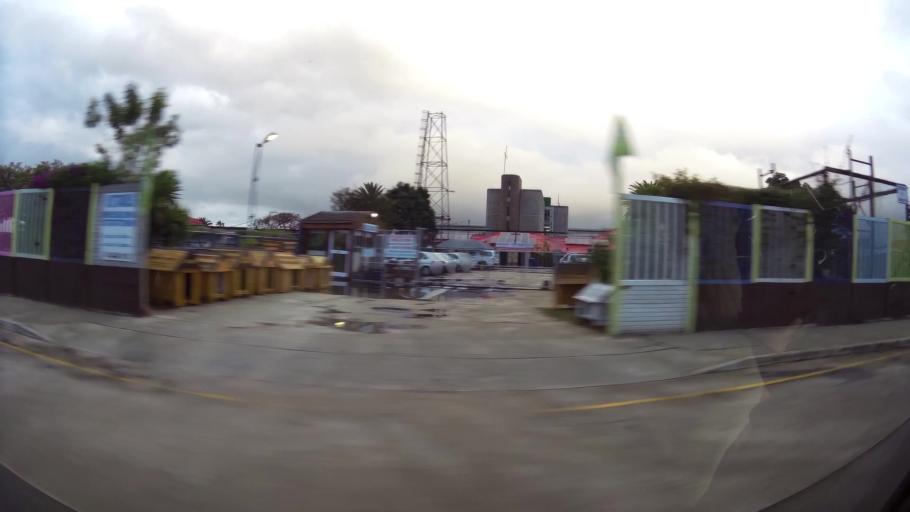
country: ZA
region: Eastern Cape
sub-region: Nelson Mandela Bay Metropolitan Municipality
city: Port Elizabeth
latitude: -33.9255
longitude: 25.6014
